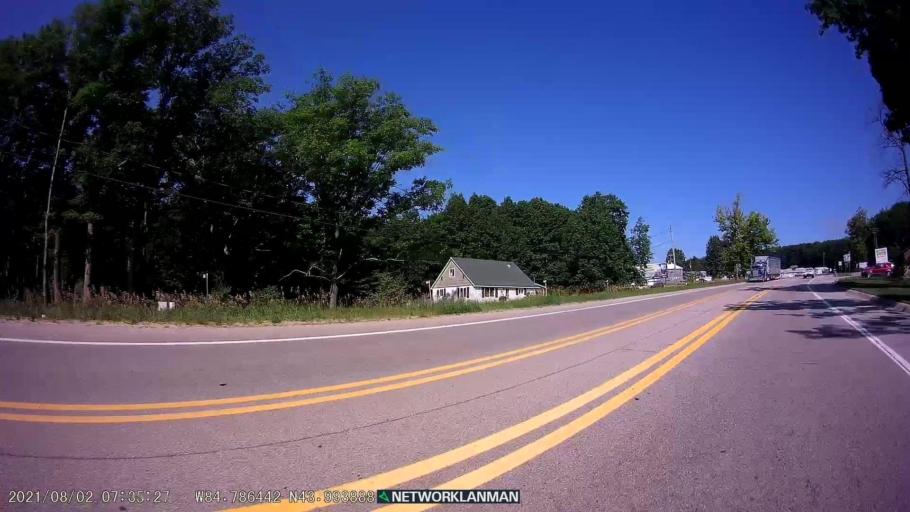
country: US
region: Michigan
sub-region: Clare County
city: Harrison
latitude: 43.9940
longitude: -84.7865
